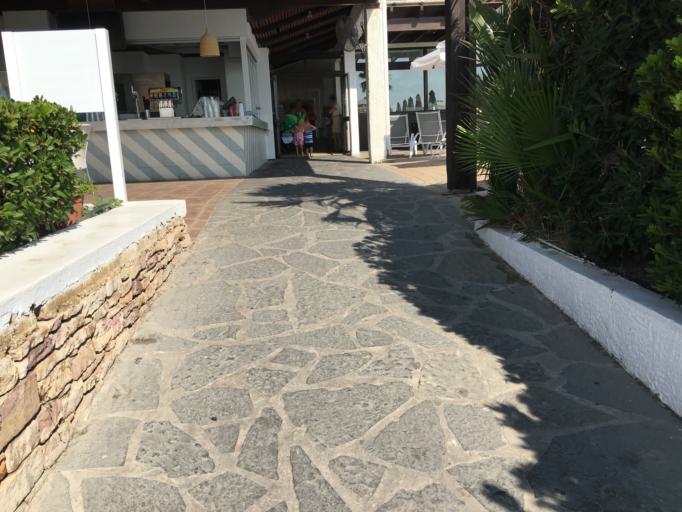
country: GR
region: South Aegean
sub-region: Nomos Dodekanisou
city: Rodos
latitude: 36.4064
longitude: 28.2283
